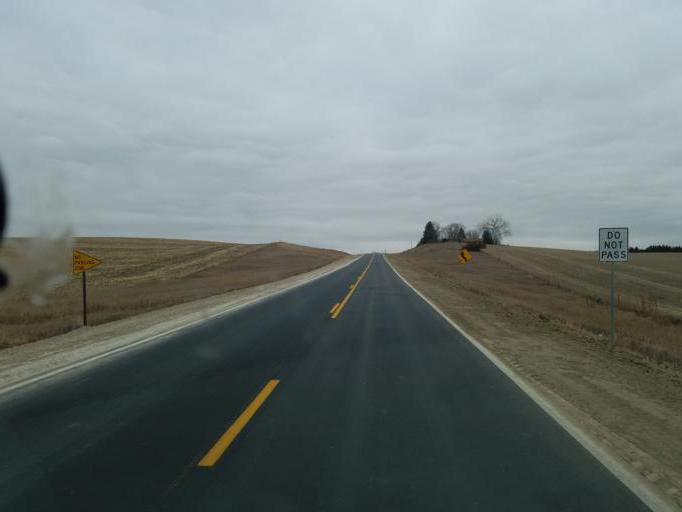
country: US
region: Nebraska
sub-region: Knox County
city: Bloomfield
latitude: 42.5978
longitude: -97.6700
